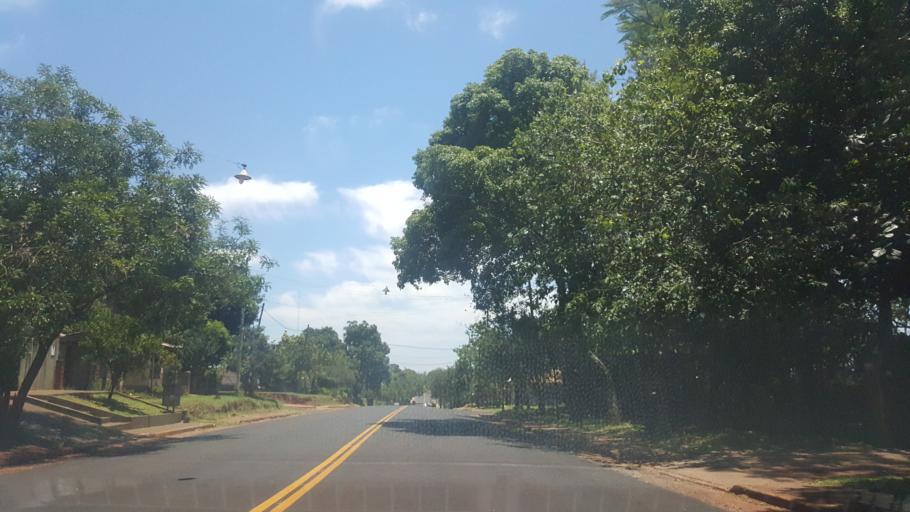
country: AR
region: Misiones
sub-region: Departamento de Capital
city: Posadas
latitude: -27.3614
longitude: -55.9235
